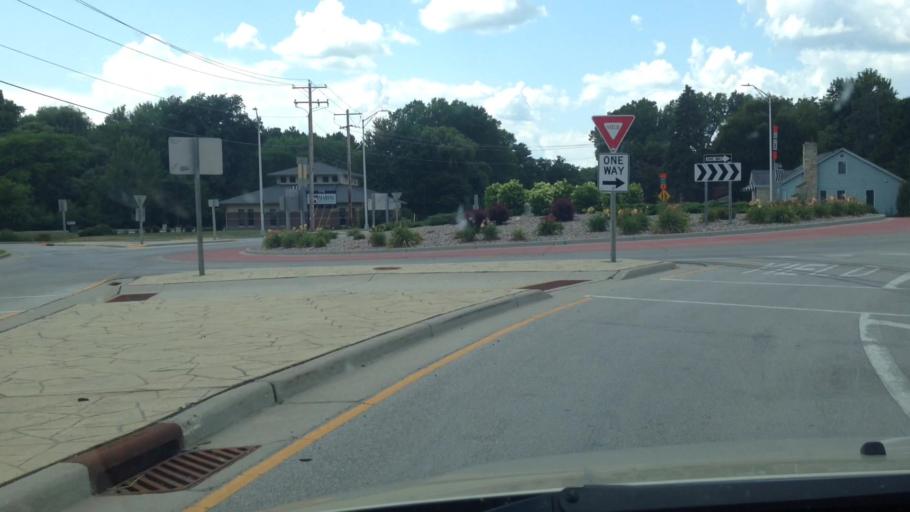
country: US
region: Wisconsin
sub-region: Brown County
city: Suamico
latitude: 44.6346
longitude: -88.0512
